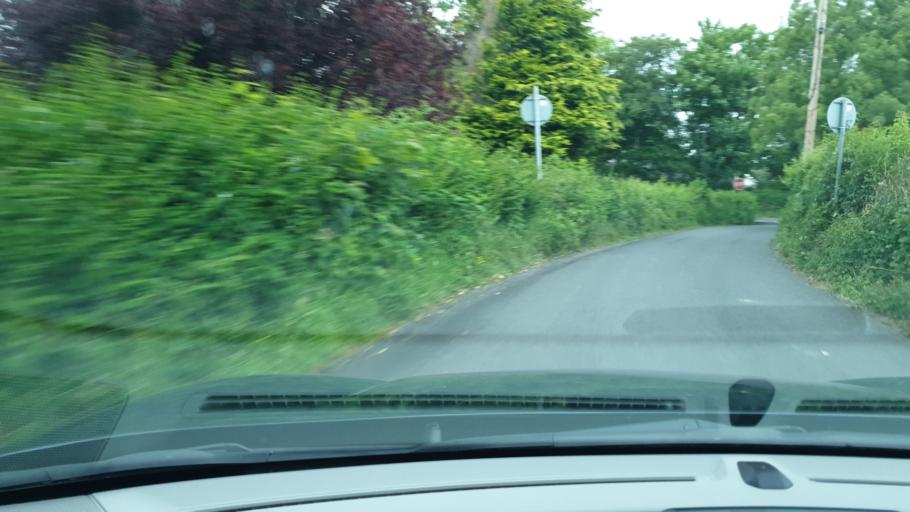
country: IE
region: Leinster
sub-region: An Mhi
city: Navan
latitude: 53.6414
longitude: -6.7249
